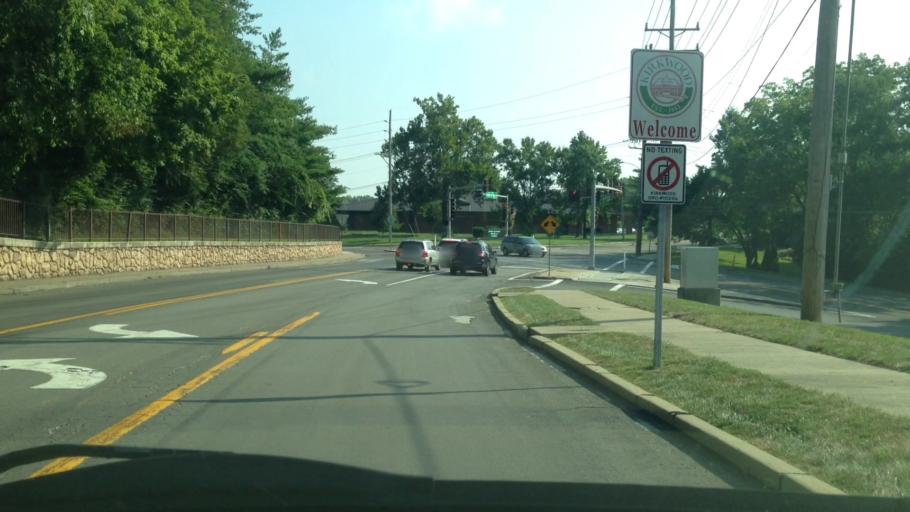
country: US
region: Missouri
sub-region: Saint Louis County
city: Des Peres
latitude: 38.5838
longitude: -90.4442
